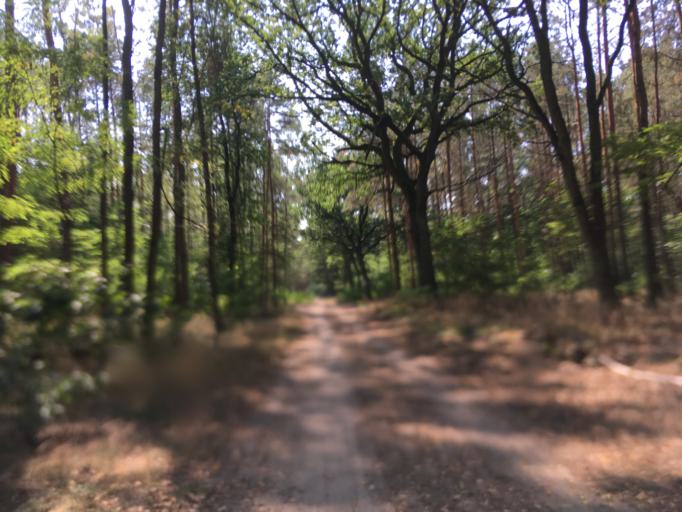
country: DE
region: Berlin
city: Friedrichshagen
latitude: 52.4701
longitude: 13.6063
